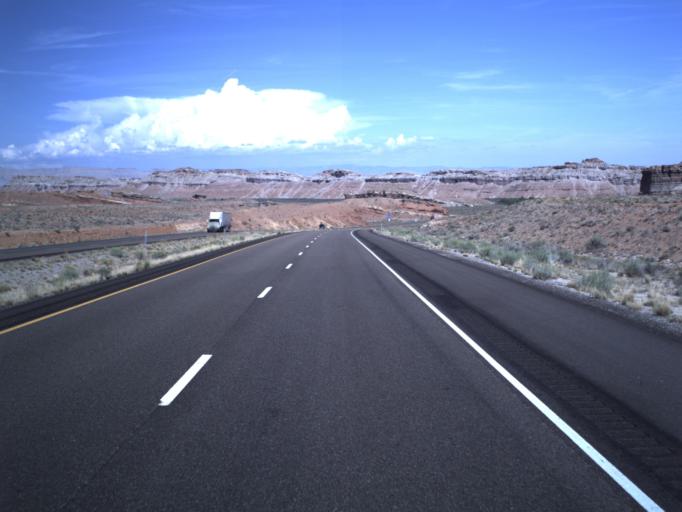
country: US
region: Utah
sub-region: Carbon County
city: East Carbon City
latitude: 38.9222
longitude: -110.4257
